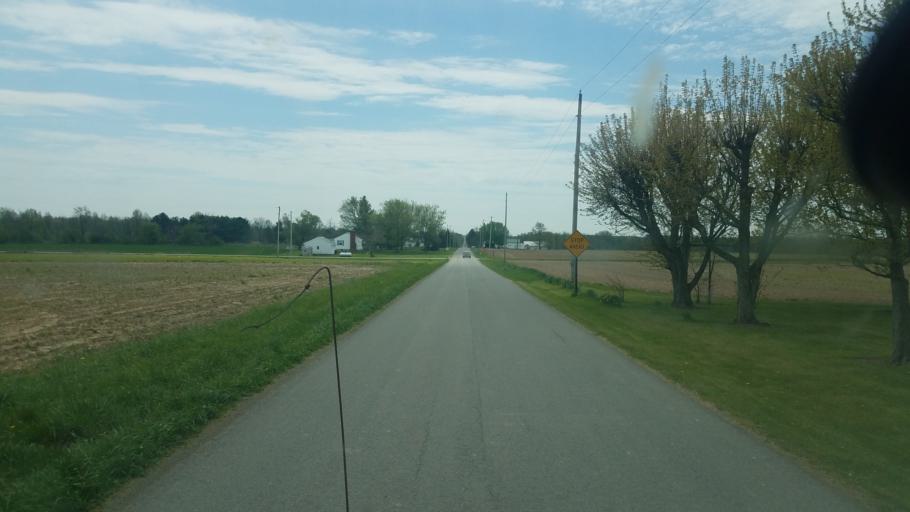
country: US
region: Ohio
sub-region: Hardin County
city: Ada
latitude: 40.7962
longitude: -83.9087
